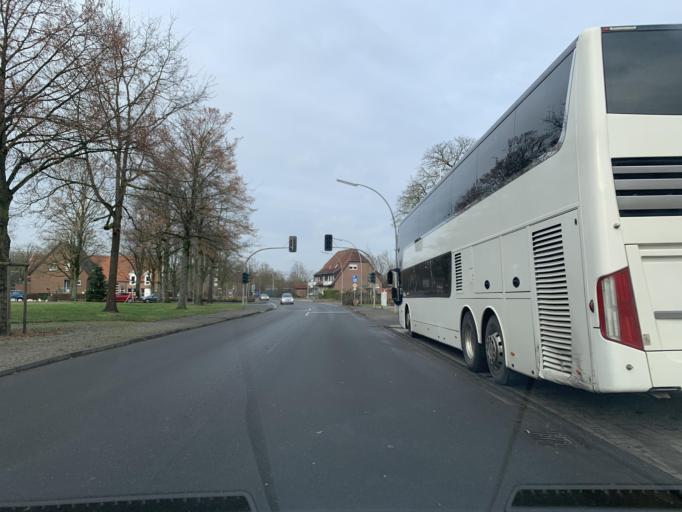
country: DE
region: North Rhine-Westphalia
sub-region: Regierungsbezirk Munster
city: Ascheberg
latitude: 51.8190
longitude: 7.5920
